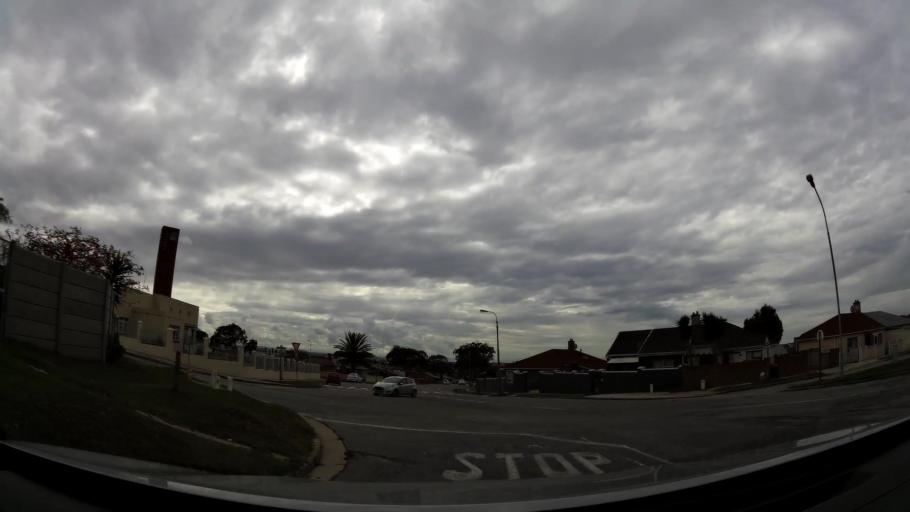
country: ZA
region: Eastern Cape
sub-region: Nelson Mandela Bay Metropolitan Municipality
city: Port Elizabeth
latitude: -33.9422
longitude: 25.5905
